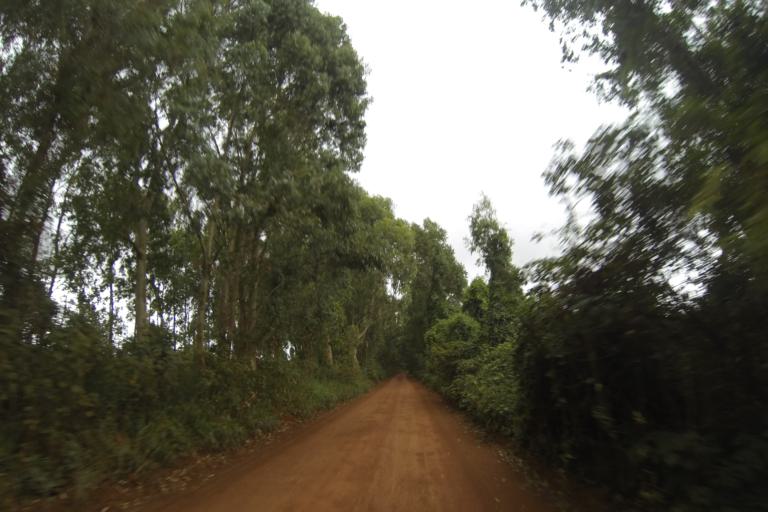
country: BR
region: Minas Gerais
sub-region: Campos Altos
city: Campos Altos
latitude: -19.8173
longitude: -46.3354
